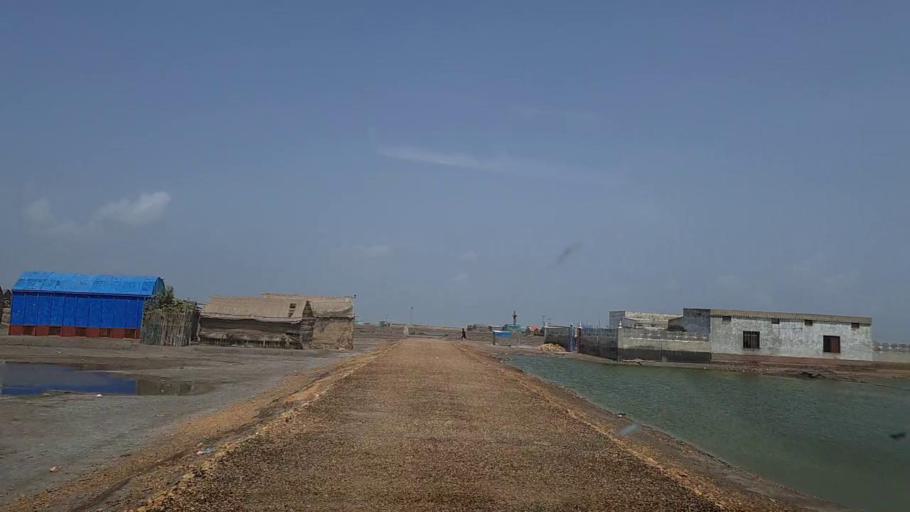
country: PK
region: Sindh
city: Keti Bandar
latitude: 24.1276
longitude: 67.4639
